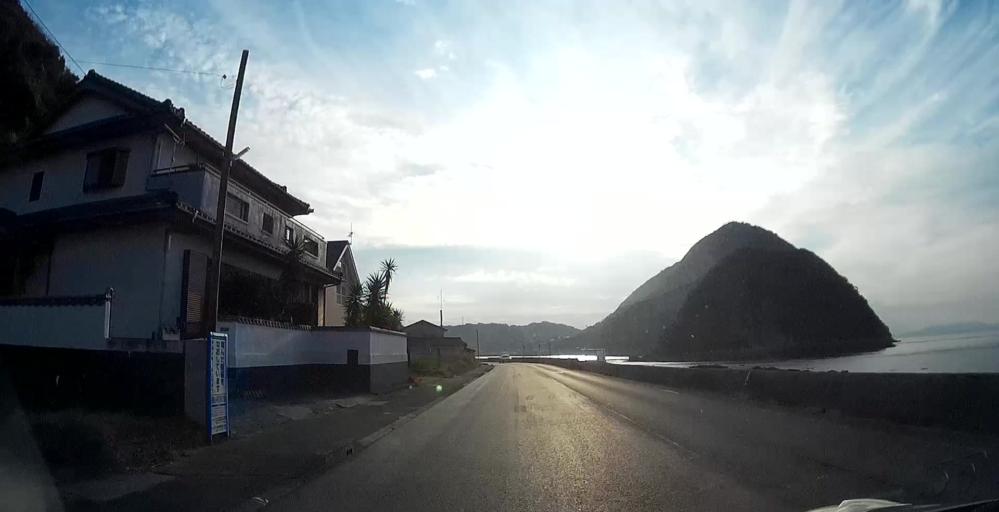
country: JP
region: Nagasaki
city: Shimabara
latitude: 32.6265
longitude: 130.4531
